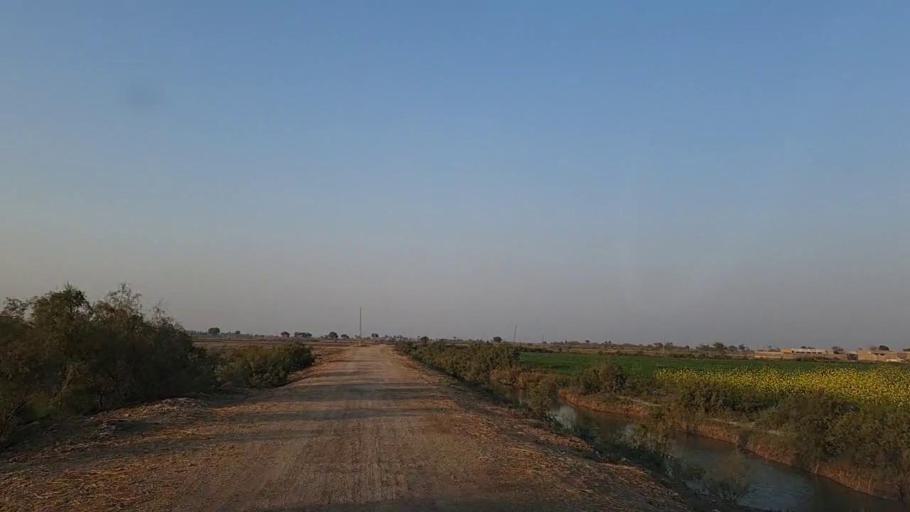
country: PK
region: Sindh
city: Bandhi
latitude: 26.5467
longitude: 68.3167
